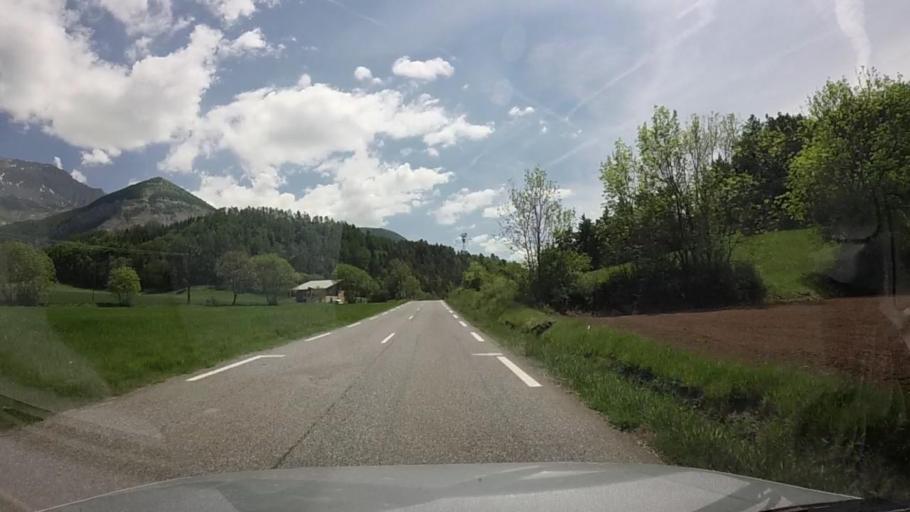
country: FR
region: Provence-Alpes-Cote d'Azur
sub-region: Departement des Alpes-de-Haute-Provence
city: Seyne-les-Alpes
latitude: 44.3200
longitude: 6.4015
